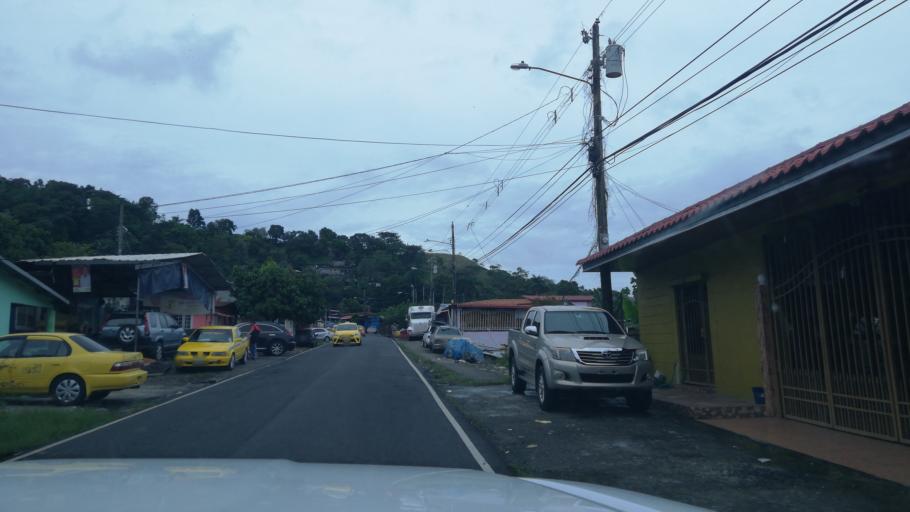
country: PA
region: Panama
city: Las Cumbres
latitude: 9.0724
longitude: -79.5140
